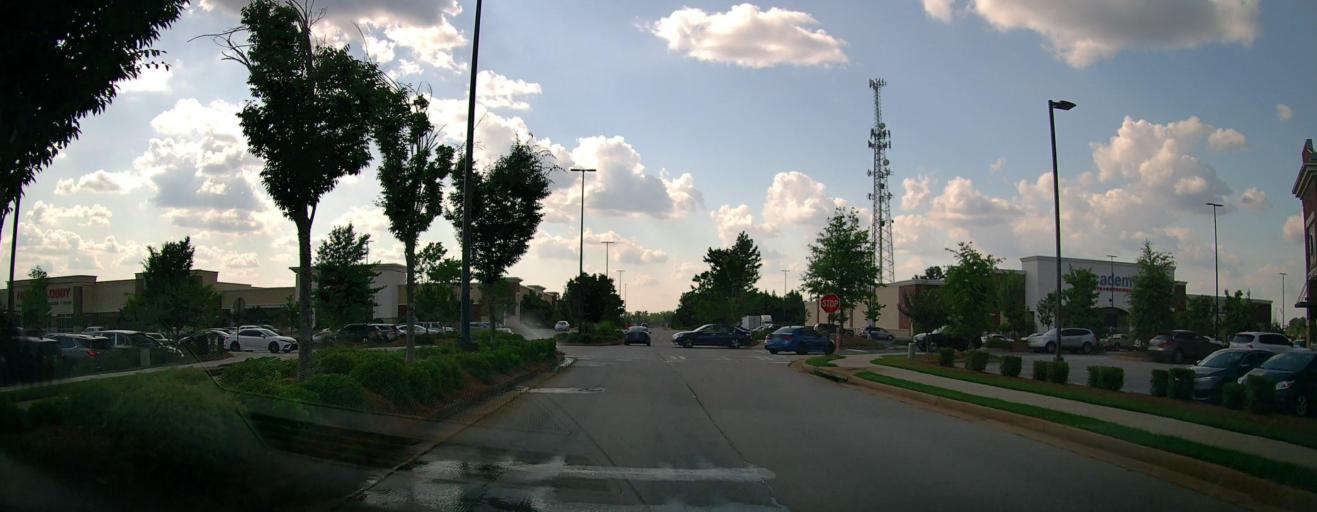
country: US
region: Georgia
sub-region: Henry County
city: McDonough
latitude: 33.4233
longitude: -84.1886
